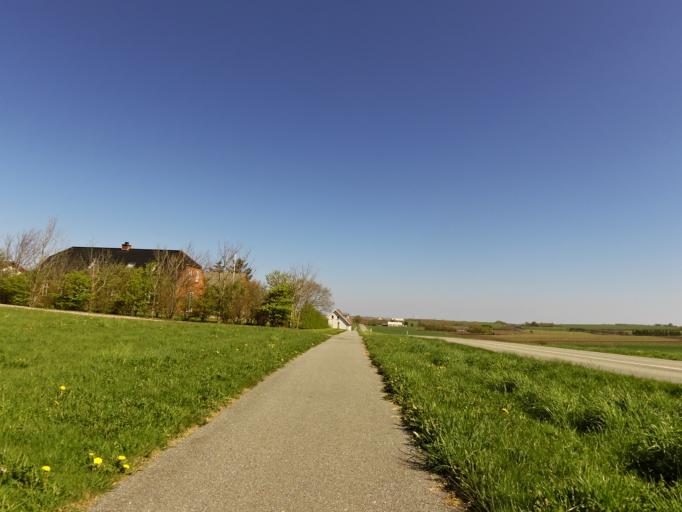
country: DK
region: Central Jutland
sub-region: Holstebro Kommune
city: Vinderup
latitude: 56.6007
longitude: 8.7401
